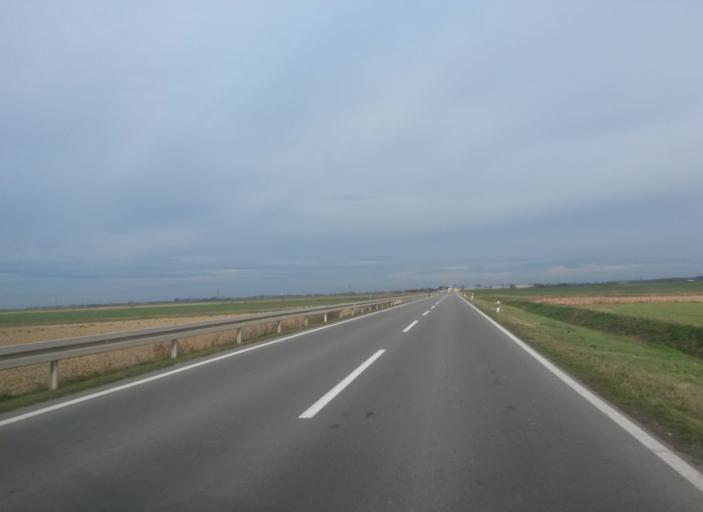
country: HR
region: Osjecko-Baranjska
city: Ovcara
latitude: 45.4822
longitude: 18.5423
